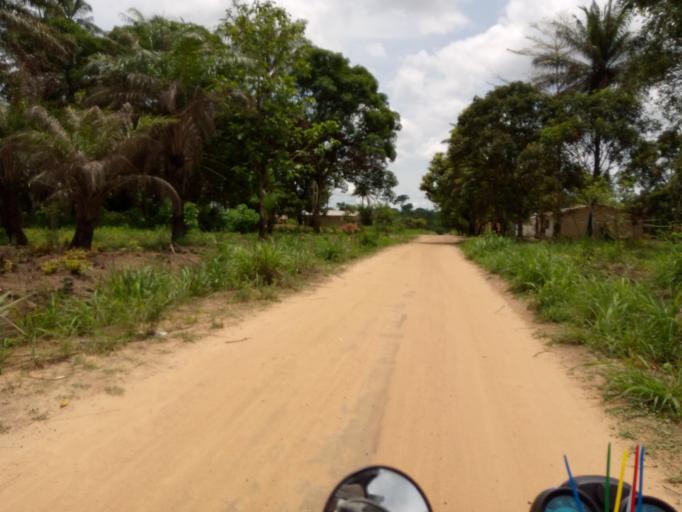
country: SL
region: Western Area
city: Waterloo
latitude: 8.3291
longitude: -12.9406
